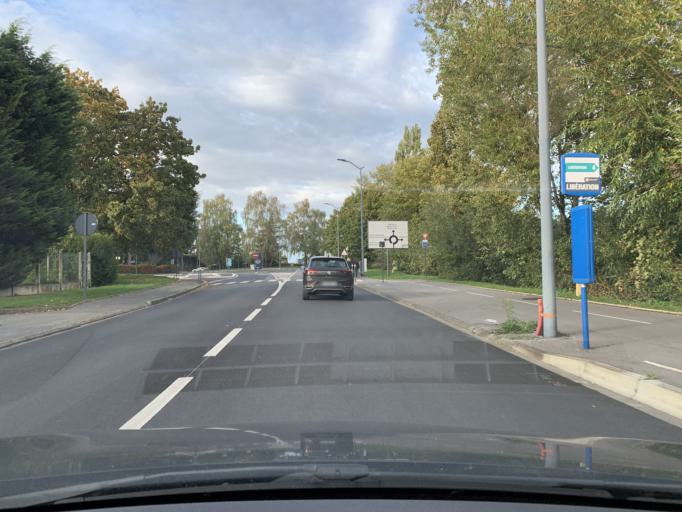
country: FR
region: Picardie
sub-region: Departement de l'Aisne
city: Harly
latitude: 49.8564
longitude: 3.3106
